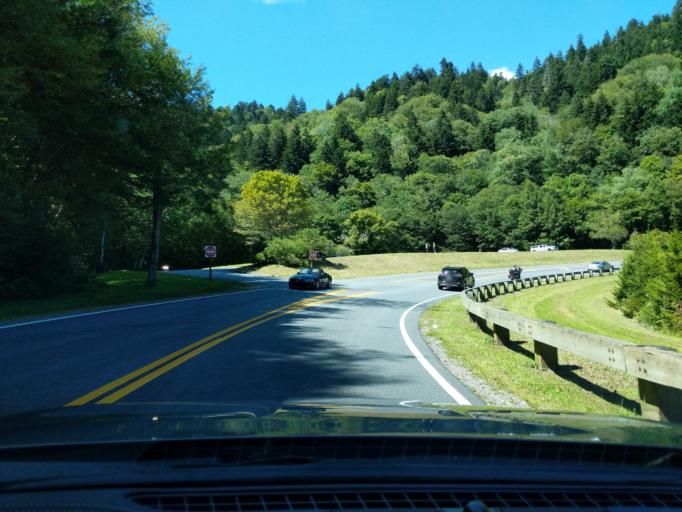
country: US
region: Tennessee
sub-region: Sevier County
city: Gatlinburg
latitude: 35.6067
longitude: -83.4359
